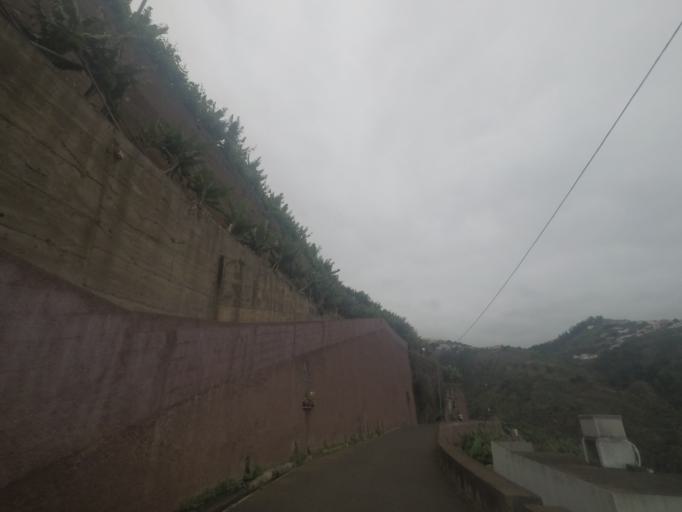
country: PT
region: Madeira
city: Camara de Lobos
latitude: 32.6600
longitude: -16.9631
